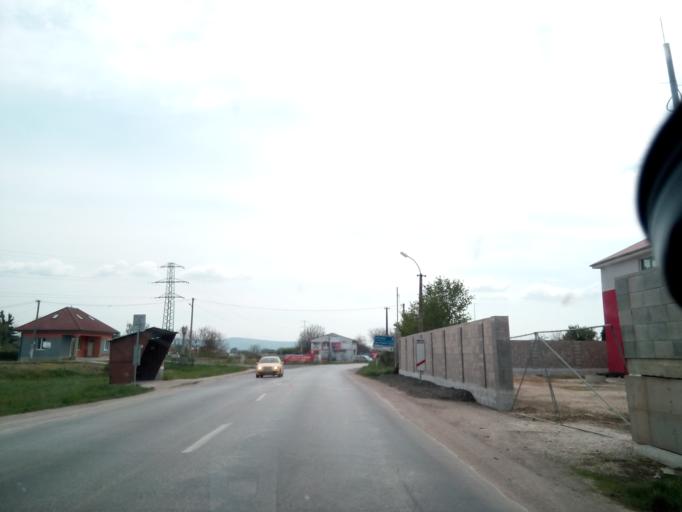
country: SK
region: Trnavsky
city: Vrbove
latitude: 48.6099
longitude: 17.7441
